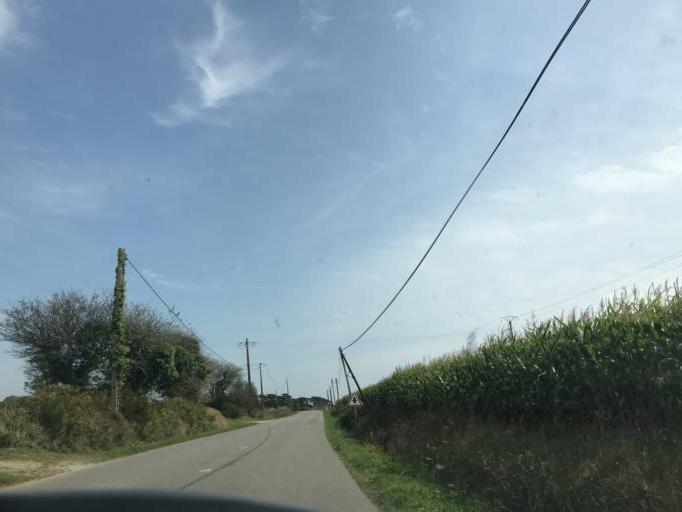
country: FR
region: Brittany
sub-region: Departement du Finistere
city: Hanvec
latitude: 48.2898
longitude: -4.1092
